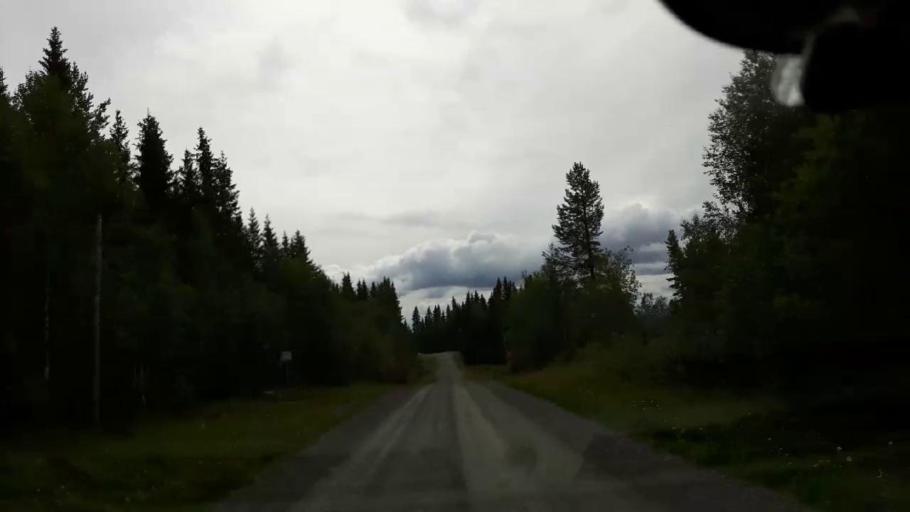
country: SE
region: Jaemtland
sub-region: Krokoms Kommun
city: Valla
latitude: 63.7093
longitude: 13.8637
